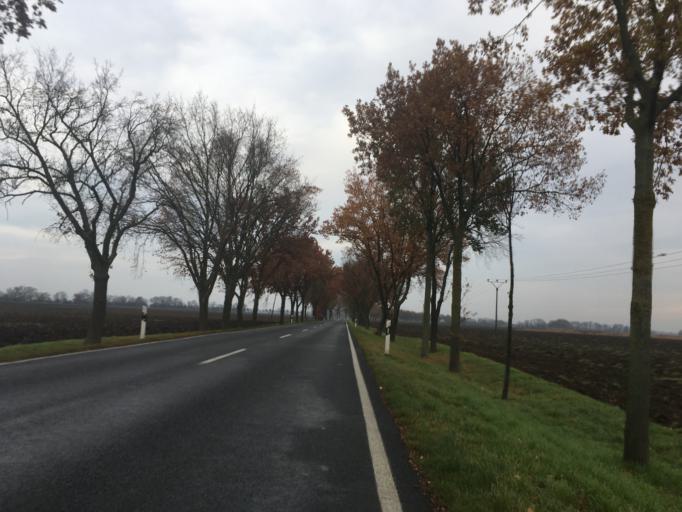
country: DE
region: Brandenburg
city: Letschin
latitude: 52.5889
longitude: 14.3432
